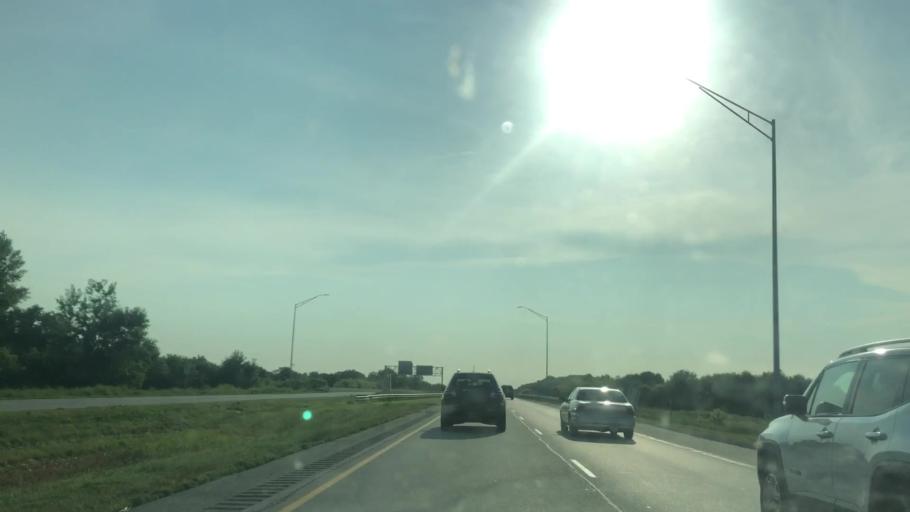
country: US
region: Iowa
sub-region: Story County
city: Ames
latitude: 42.0063
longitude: -93.5923
